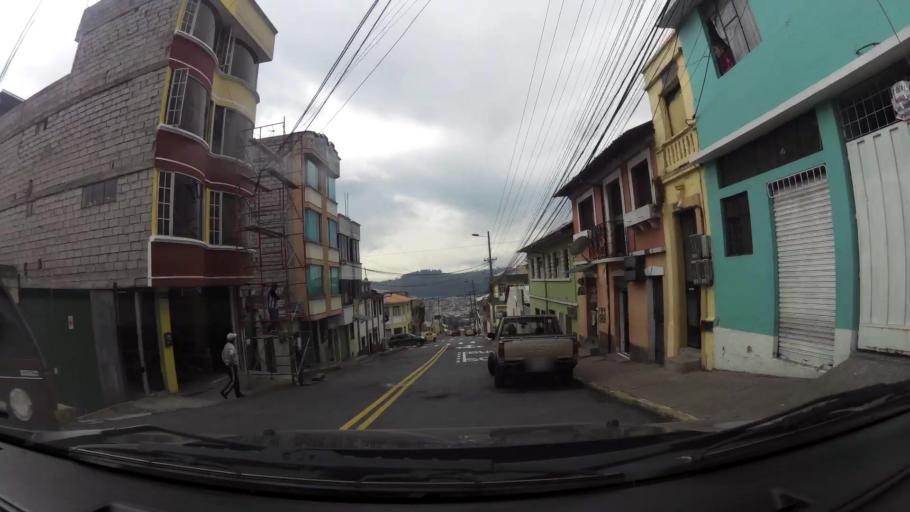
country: EC
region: Pichincha
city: Quito
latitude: -0.2112
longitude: -78.5124
